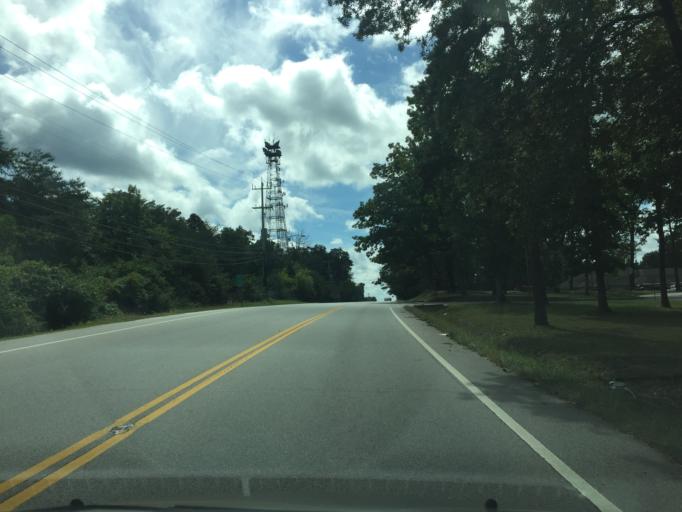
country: US
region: Tennessee
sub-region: Hamilton County
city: Signal Mountain
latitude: 35.1324
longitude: -85.3328
